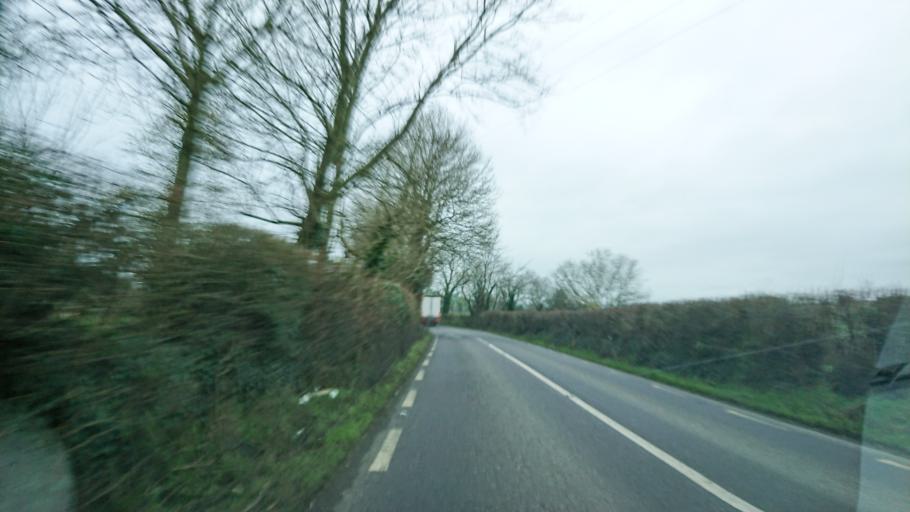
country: IE
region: Munster
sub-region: County Cork
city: Bandon
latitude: 51.7452
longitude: -8.8231
